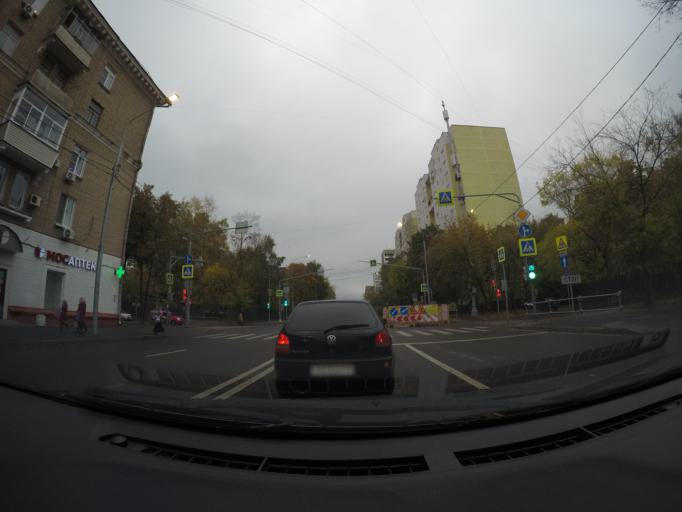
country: RU
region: Moskovskaya
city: Novogireyevo
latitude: 55.7568
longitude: 37.8017
